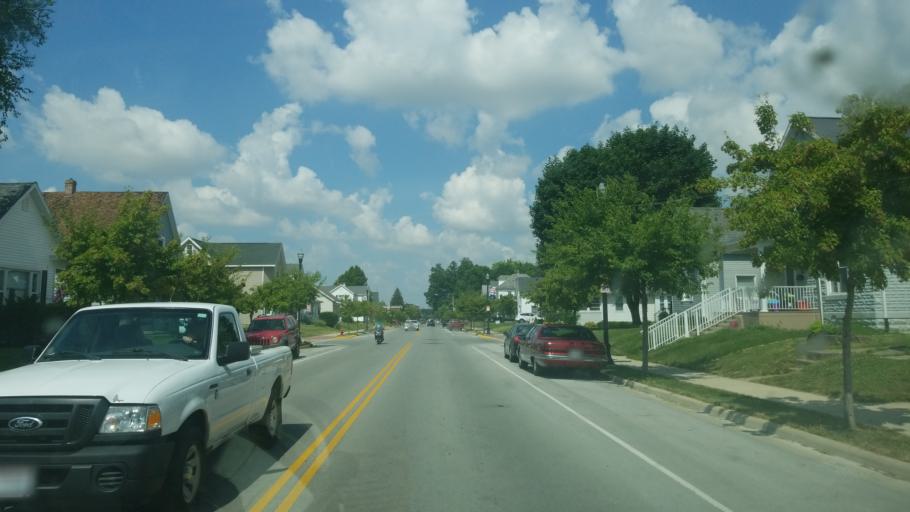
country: US
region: Ohio
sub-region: Auglaize County
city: Wapakoneta
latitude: 40.5704
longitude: -84.1854
